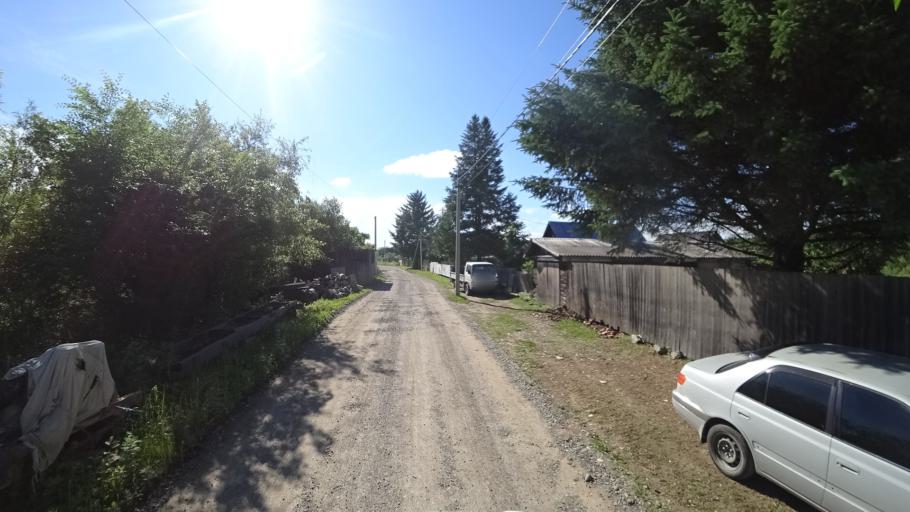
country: RU
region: Khabarovsk Krai
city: Khor
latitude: 47.8865
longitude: 135.0151
